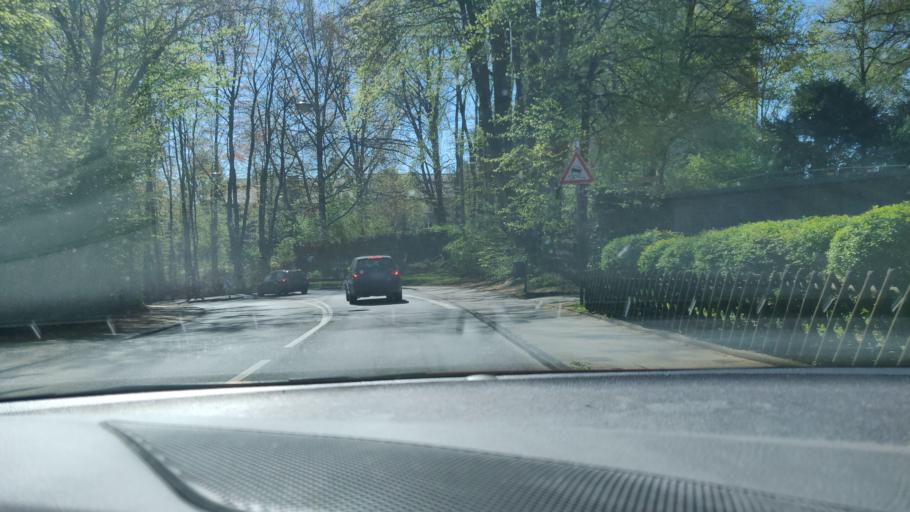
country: DE
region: North Rhine-Westphalia
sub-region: Regierungsbezirk Dusseldorf
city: Mettmann
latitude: 51.2501
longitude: 6.9687
